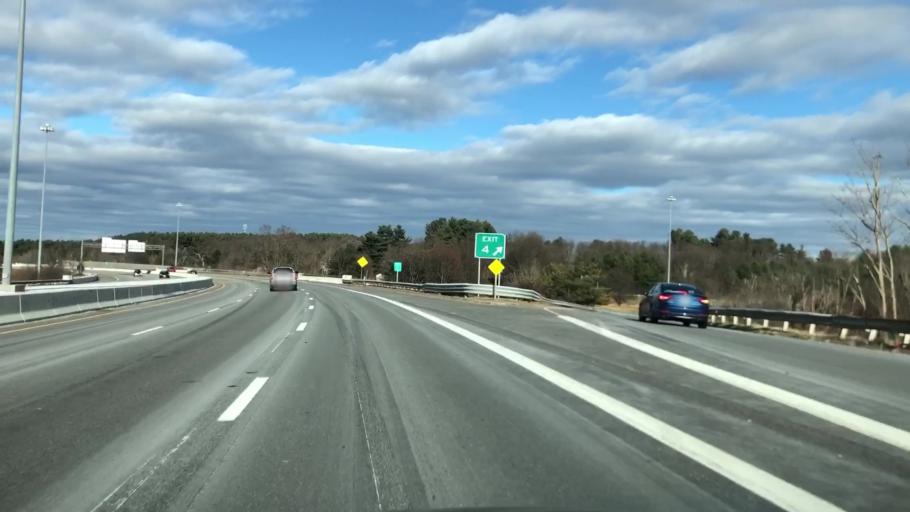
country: US
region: Massachusetts
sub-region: Worcester County
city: West Boylston
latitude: 42.3342
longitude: -71.7981
